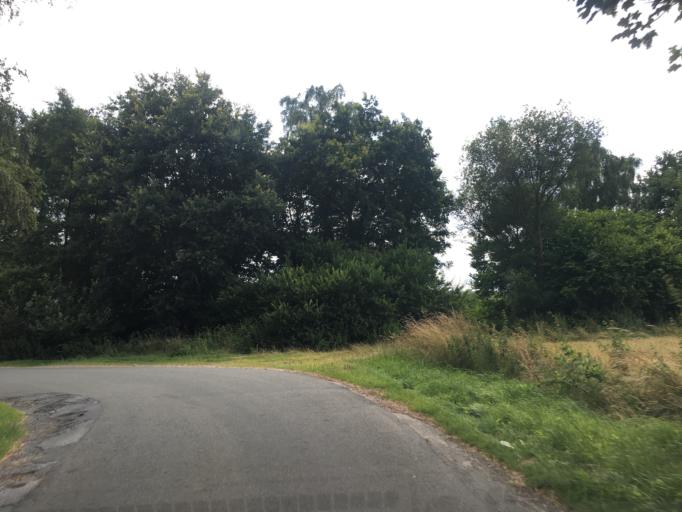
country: DE
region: North Rhine-Westphalia
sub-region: Regierungsbezirk Munster
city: Greven
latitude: 52.0327
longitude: 7.6233
